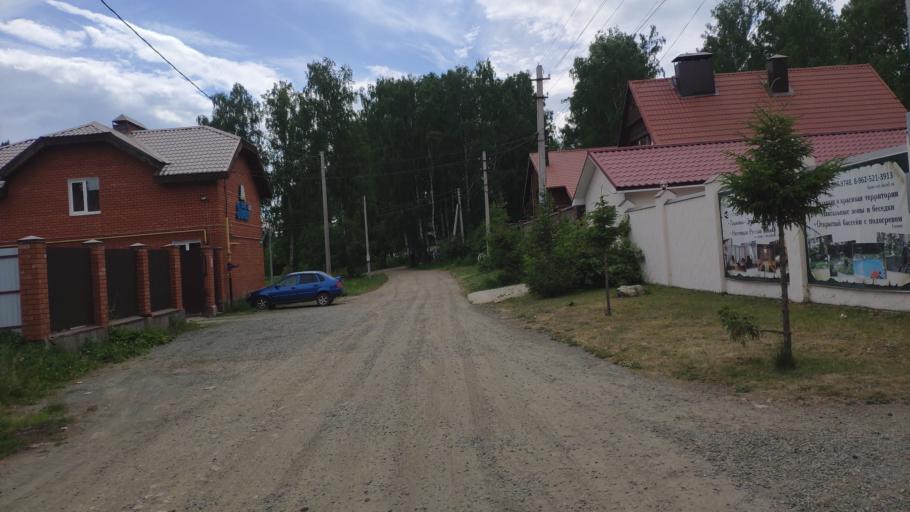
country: RU
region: Bashkortostan
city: Abzakovo
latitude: 53.8133
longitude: 58.6350
